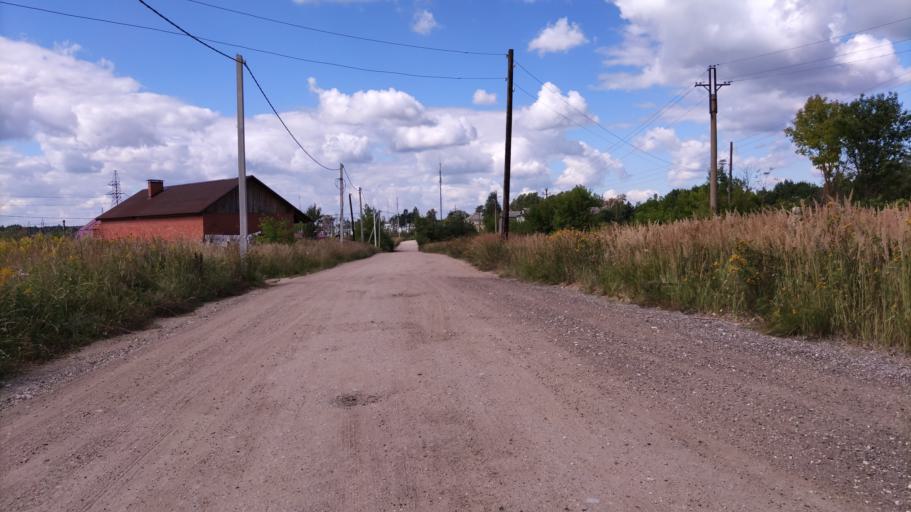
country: RU
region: Tverskaya
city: Rzhev
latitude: 56.2373
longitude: 34.3255
